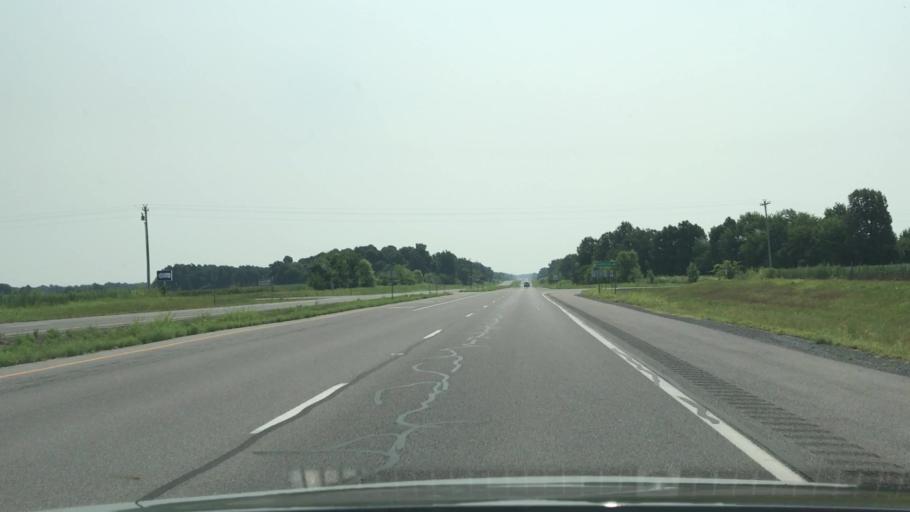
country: US
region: Kentucky
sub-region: Graves County
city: Mayfield
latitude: 36.6751
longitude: -88.5160
